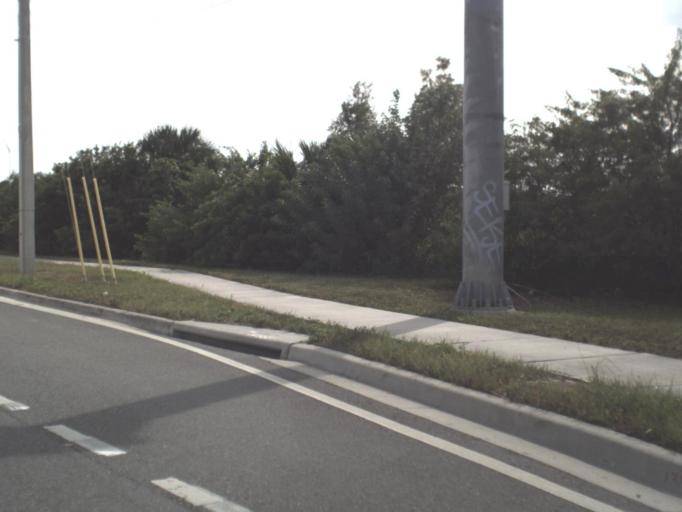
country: US
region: Florida
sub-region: Orange County
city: Conway
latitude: 28.4504
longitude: -81.2658
